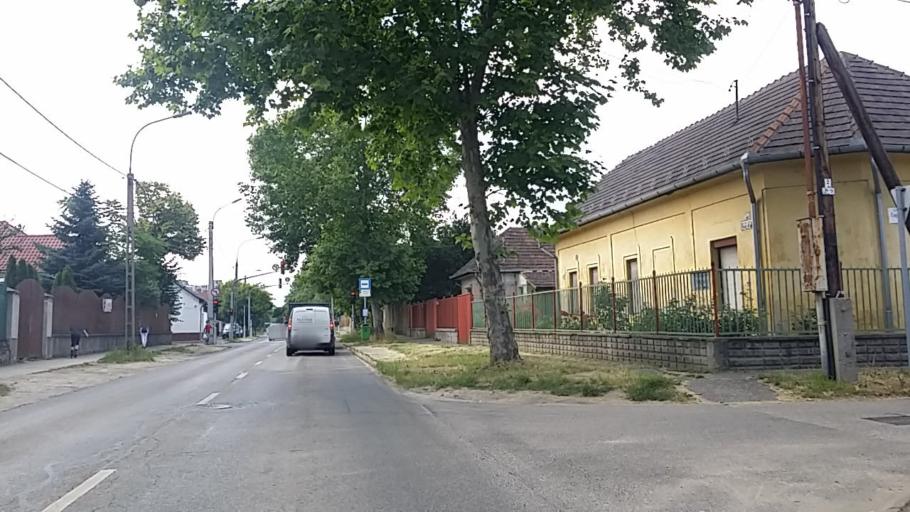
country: HU
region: Budapest
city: Budapest XXI. keruelet
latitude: 47.4157
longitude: 19.0730
